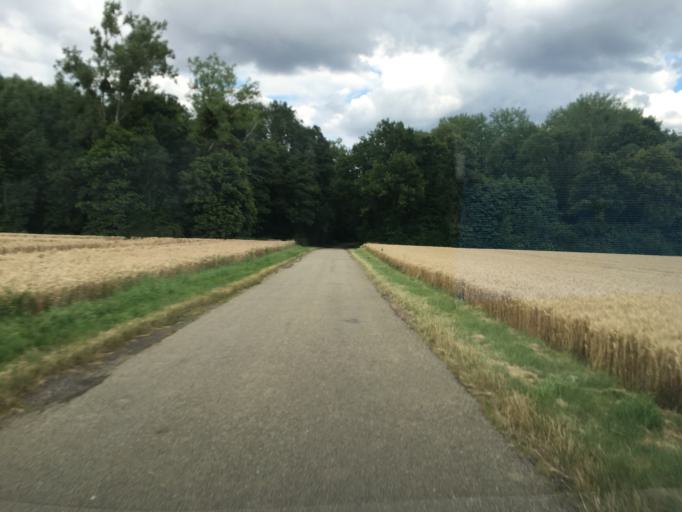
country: FR
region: Bourgogne
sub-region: Departement de l'Yonne
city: Charbuy
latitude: 47.8266
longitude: 3.4124
